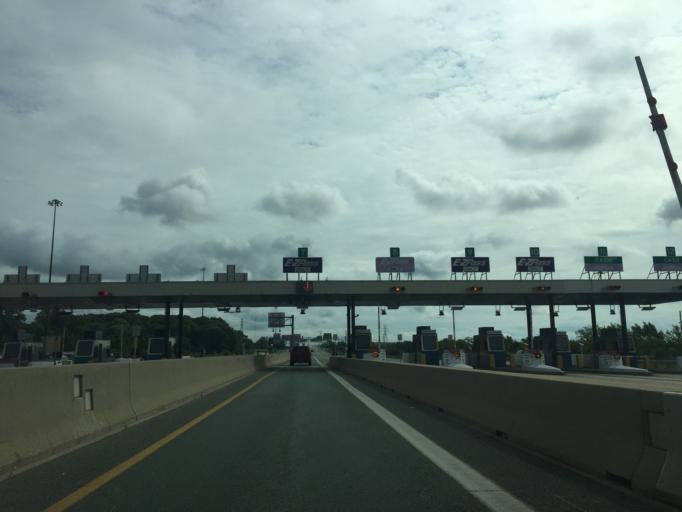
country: US
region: Maryland
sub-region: Baltimore County
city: Dundalk
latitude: 39.2295
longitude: -76.5110
